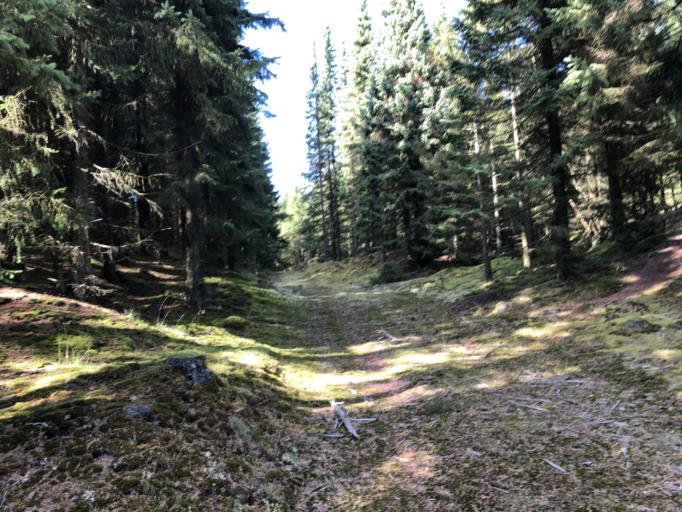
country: DK
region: Central Jutland
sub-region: Holstebro Kommune
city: Holstebro
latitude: 56.2500
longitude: 8.4926
